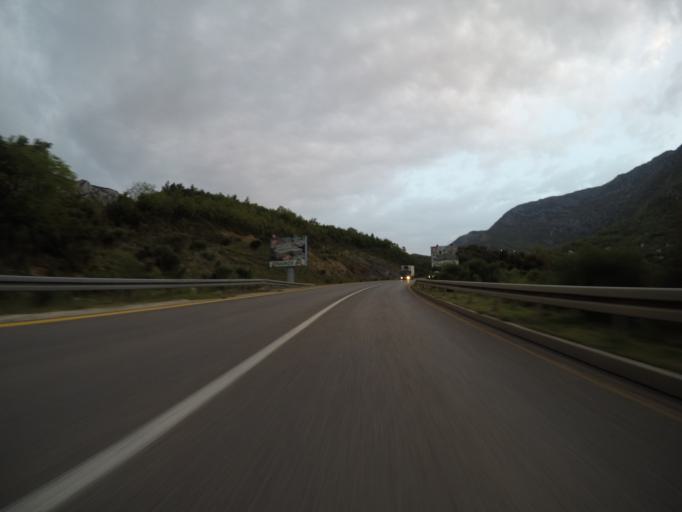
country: ME
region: Bar
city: Sutomore
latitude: 42.1541
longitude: 19.0288
